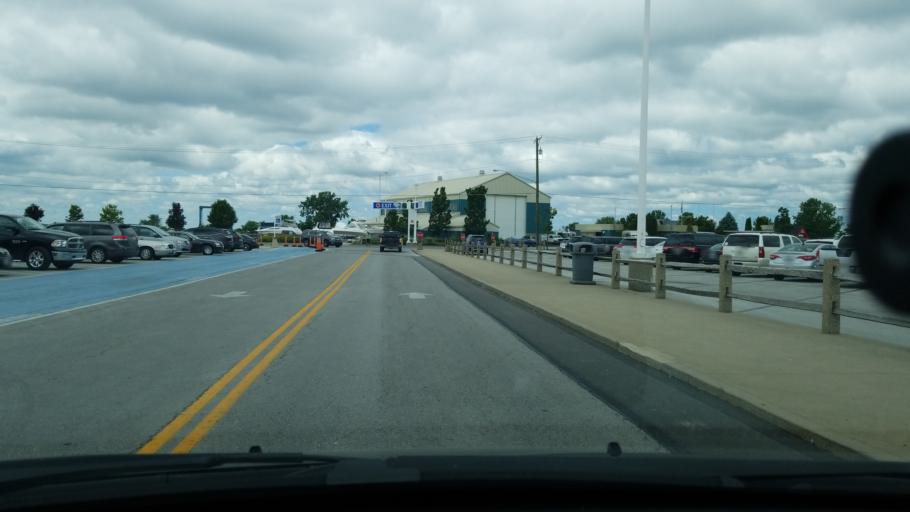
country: US
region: Ohio
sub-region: Erie County
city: Sandusky
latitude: 41.4769
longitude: -82.6793
